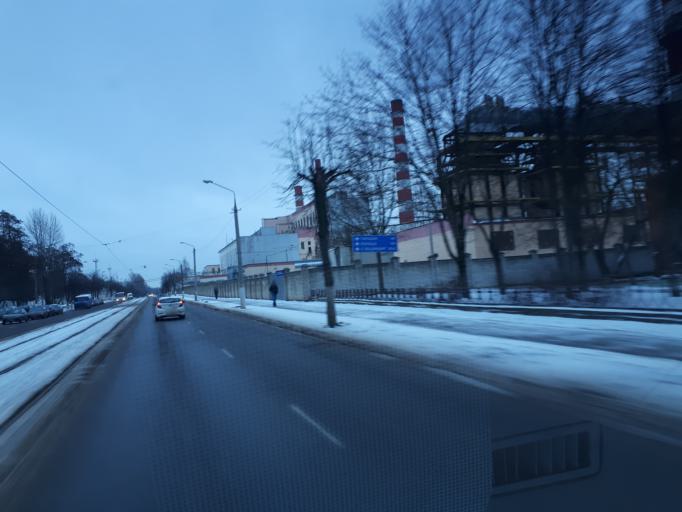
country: BY
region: Vitebsk
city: Vitebsk
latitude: 55.1679
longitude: 30.1310
